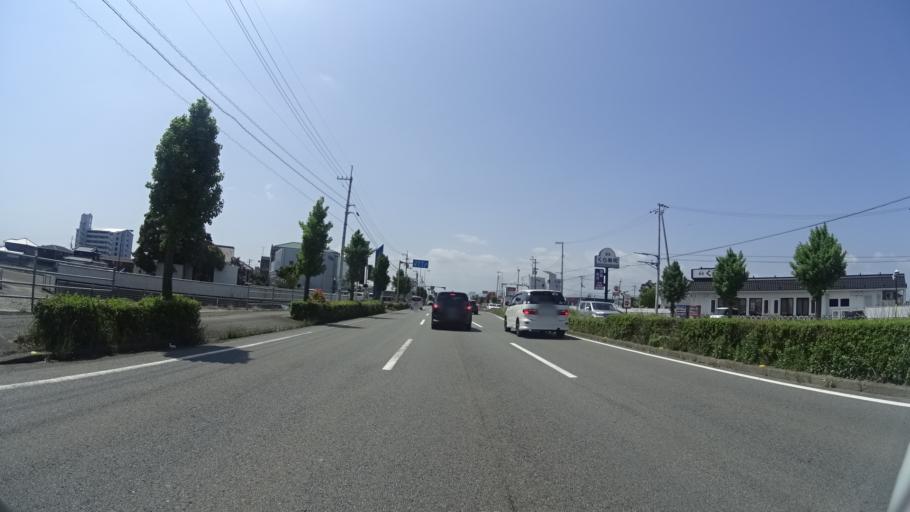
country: JP
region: Tokushima
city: Tokushima-shi
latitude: 34.1094
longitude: 134.5769
